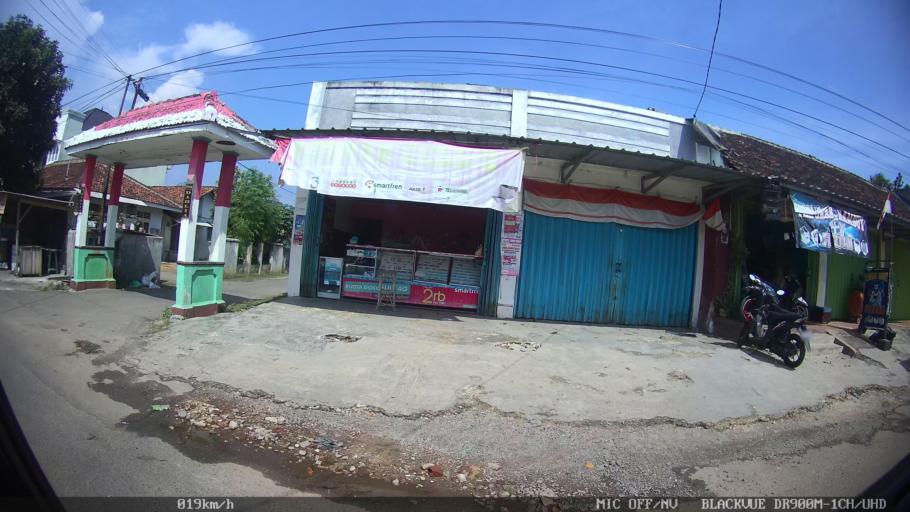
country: ID
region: Lampung
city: Kedaton
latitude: -5.3989
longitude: 105.2350
